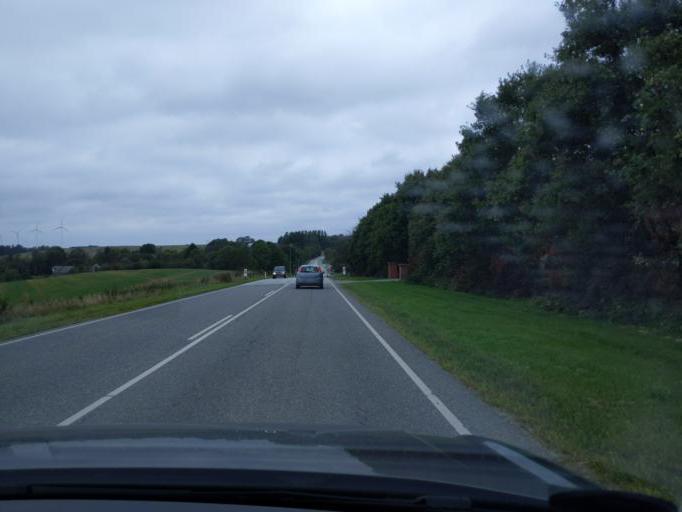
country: DK
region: North Denmark
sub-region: Mariagerfjord Kommune
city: Hobro
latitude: 56.5676
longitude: 9.8265
